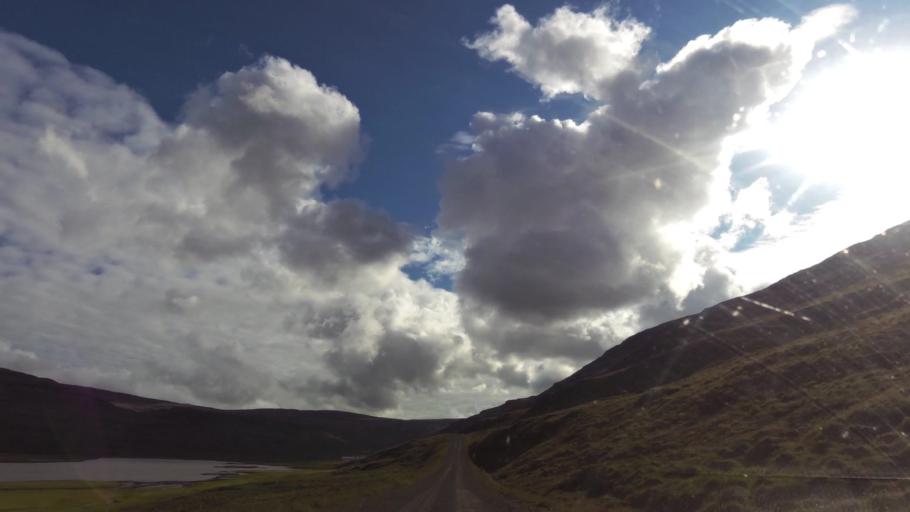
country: IS
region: West
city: Olafsvik
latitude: 65.5706
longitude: -24.1641
